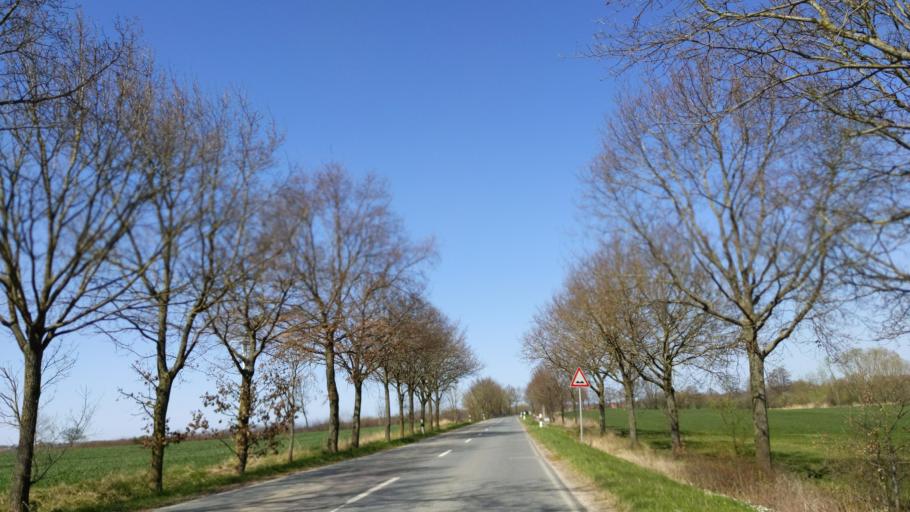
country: DE
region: Schleswig-Holstein
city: Ahrensbok
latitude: 54.0041
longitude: 10.6560
